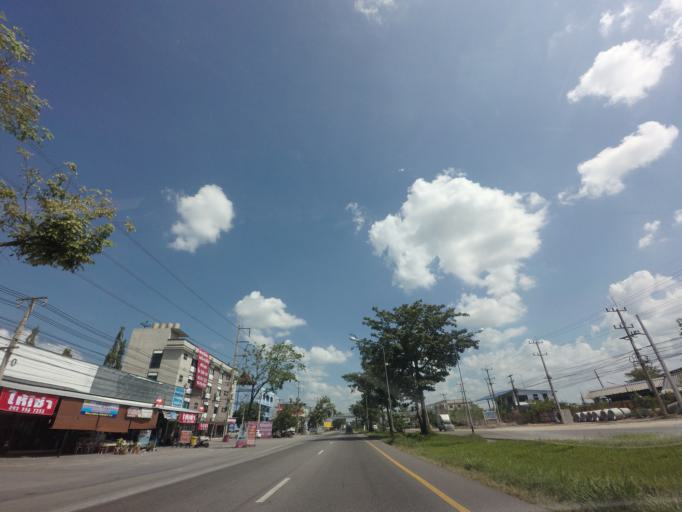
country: TH
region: Chon Buri
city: Ban Bueng
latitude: 13.3021
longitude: 101.1424
